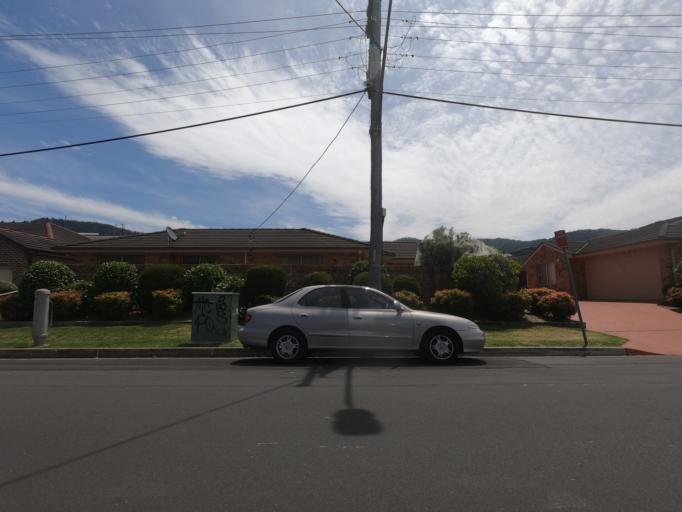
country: AU
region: New South Wales
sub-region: Wollongong
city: Mount Ousley
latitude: -34.3893
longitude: 150.8806
